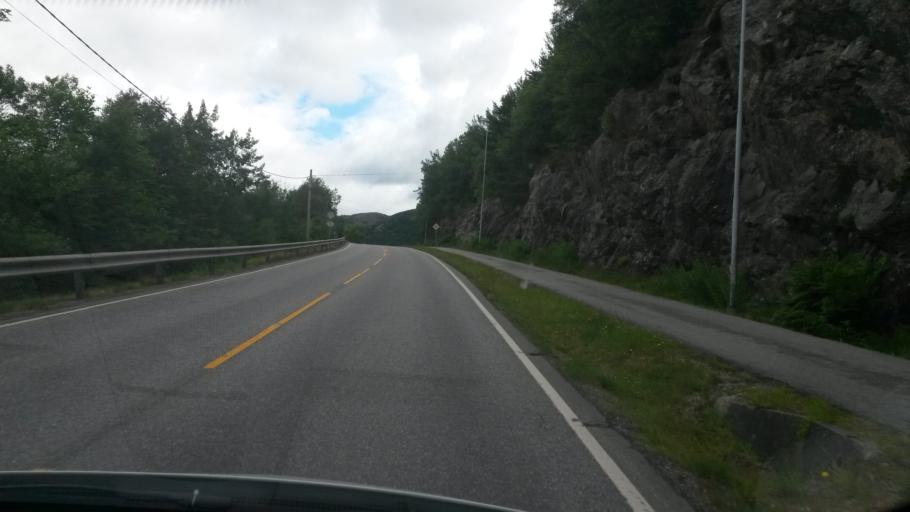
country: NO
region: Rogaland
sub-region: Sandnes
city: Sandnes
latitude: 58.8746
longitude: 5.7654
